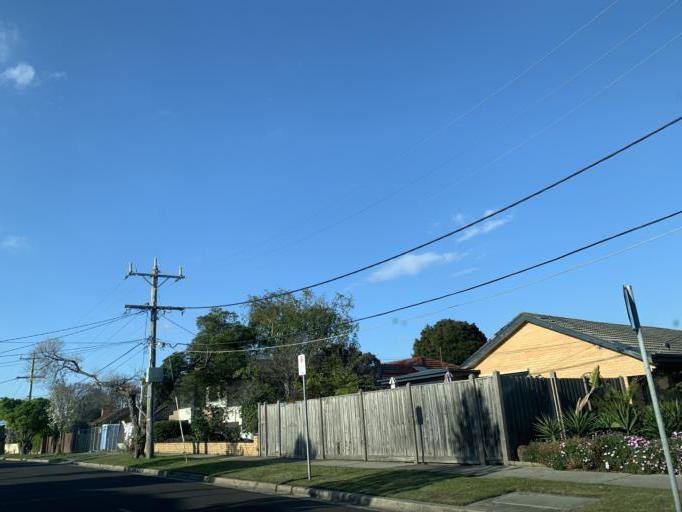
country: AU
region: Victoria
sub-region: Kingston
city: Mordialloc
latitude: -37.9876
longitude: 145.0845
